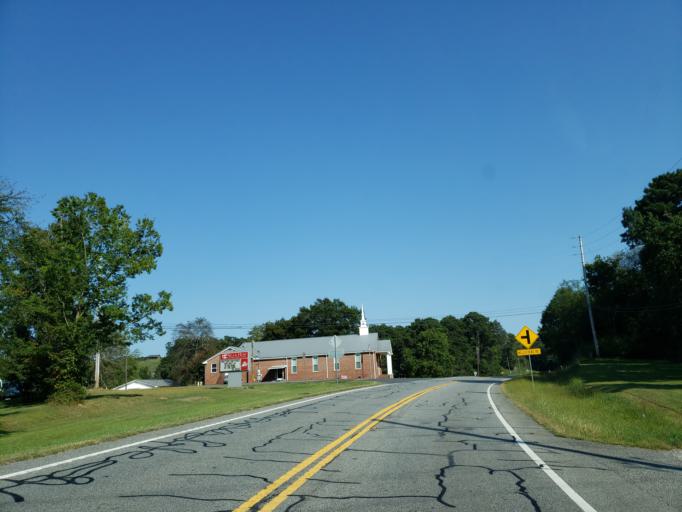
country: US
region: Georgia
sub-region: Whitfield County
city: Varnell
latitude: 34.8989
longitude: -85.0418
